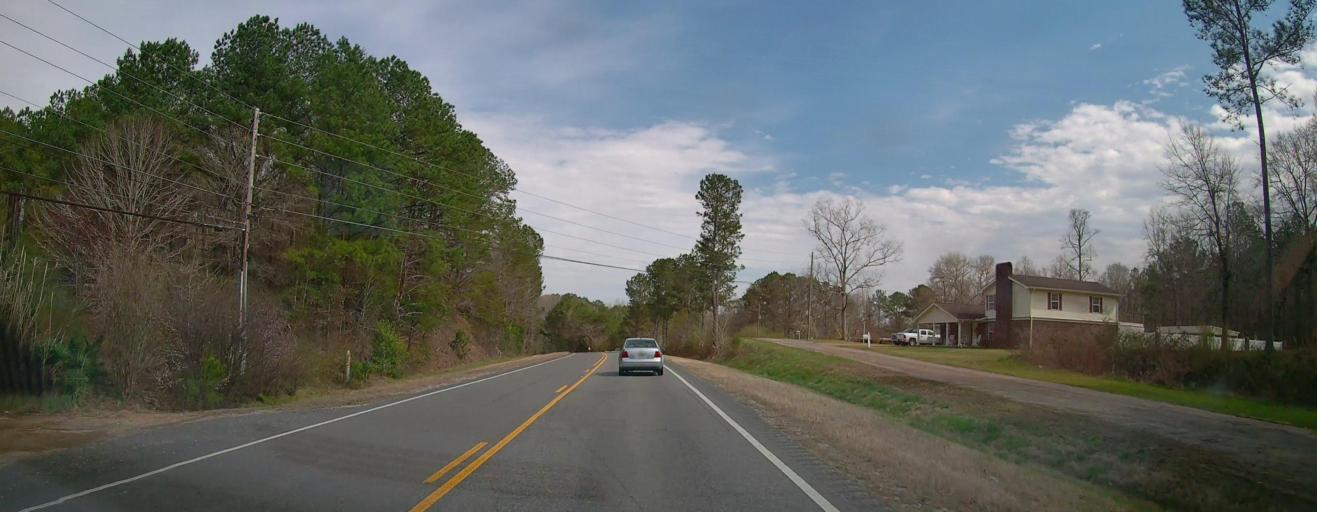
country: US
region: Alabama
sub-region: Walker County
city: Carbon Hill
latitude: 33.9192
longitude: -87.5803
